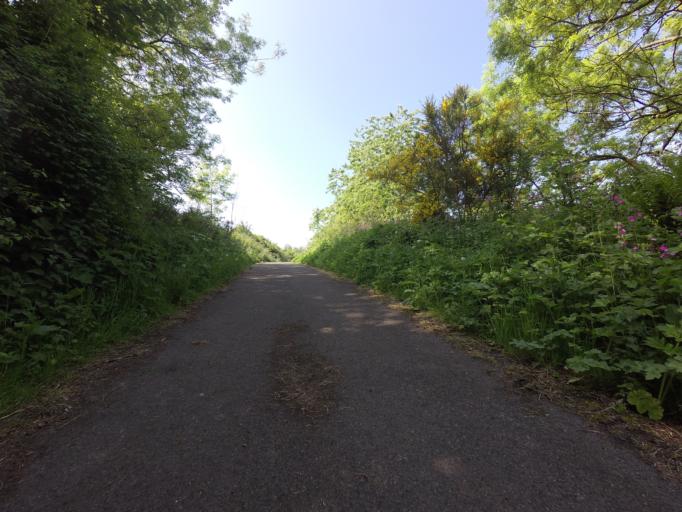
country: GB
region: Scotland
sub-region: Fife
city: Townhill
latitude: 56.0938
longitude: -3.4419
